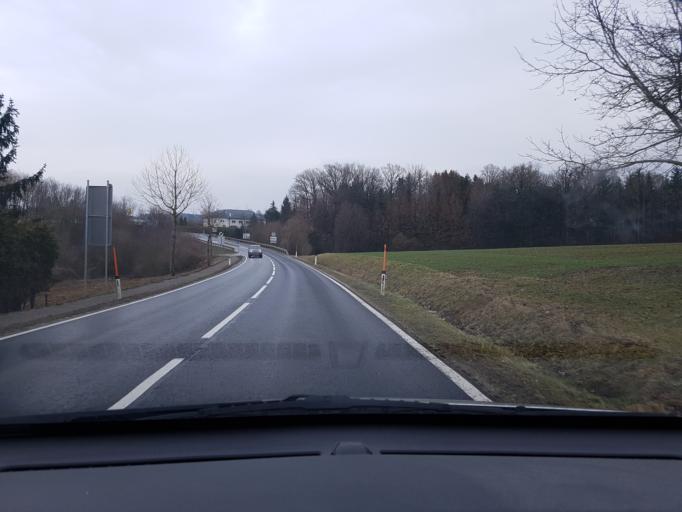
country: AT
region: Upper Austria
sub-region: Steyr Stadt
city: Steyr
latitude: 48.0804
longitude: 14.3716
